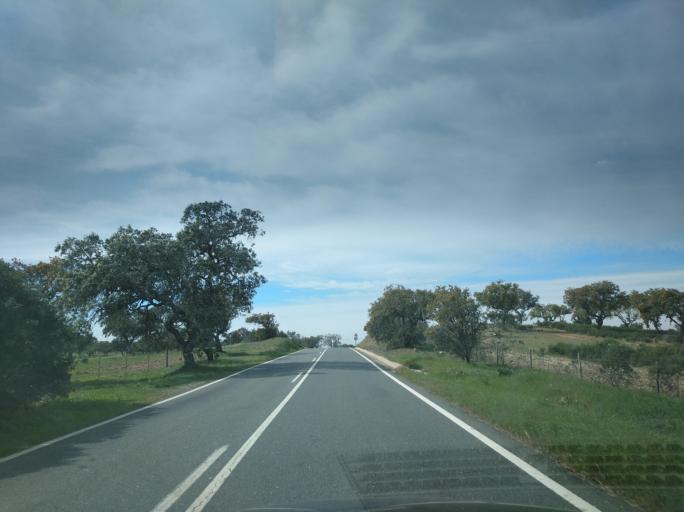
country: PT
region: Beja
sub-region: Mertola
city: Mertola
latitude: 37.7408
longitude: -7.7867
